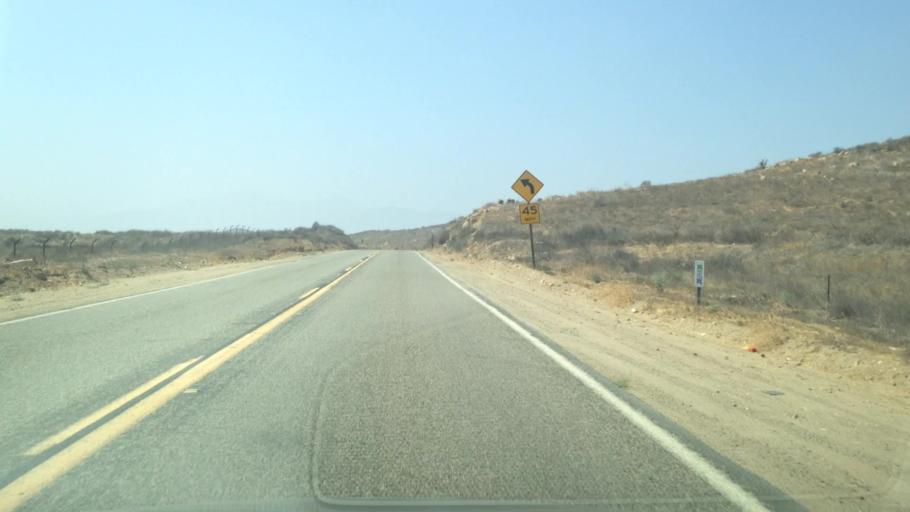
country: US
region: California
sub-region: Riverside County
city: El Cerrito
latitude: 33.8472
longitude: -117.4619
